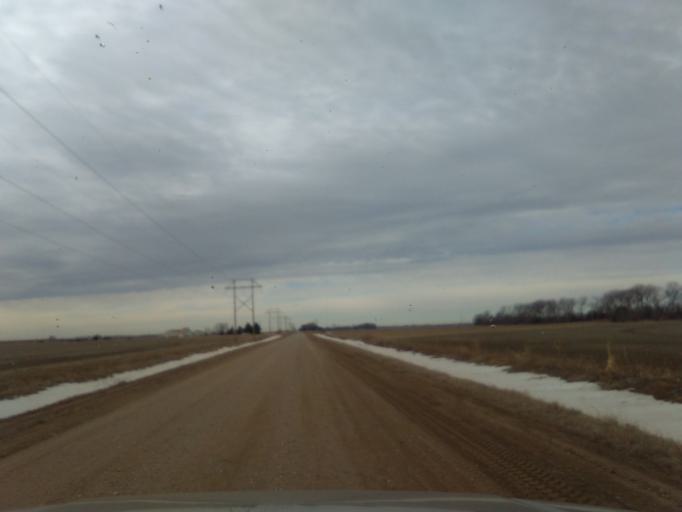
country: US
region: Nebraska
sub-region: Buffalo County
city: Gibbon
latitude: 40.6550
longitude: -98.7869
